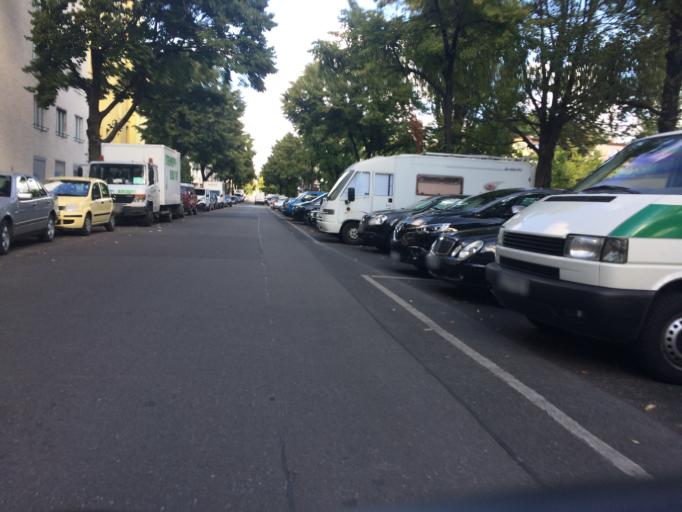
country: DE
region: Berlin
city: Gesundbrunnen
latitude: 52.5423
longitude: 13.3954
